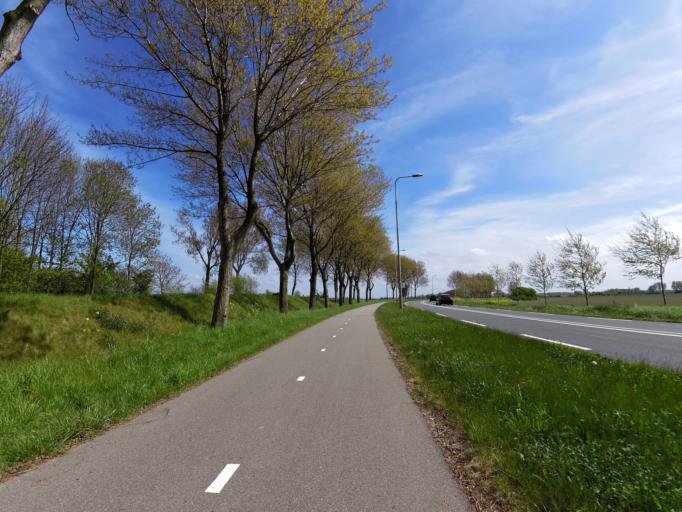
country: NL
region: South Holland
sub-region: Gemeente Hellevoetsluis
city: Nieuw-Helvoet
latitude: 51.8724
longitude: 4.0937
